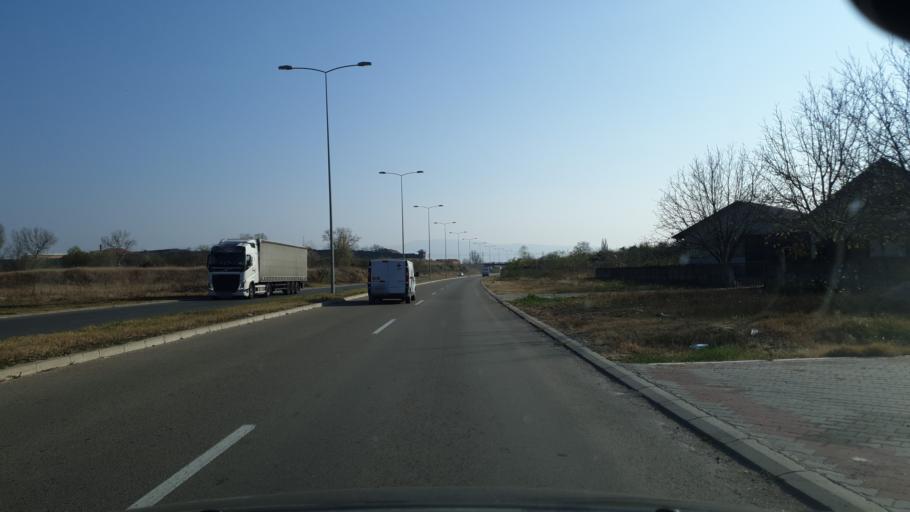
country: RS
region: Central Serbia
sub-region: Nisavski Okrug
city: Nis
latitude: 43.3231
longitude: 21.8258
